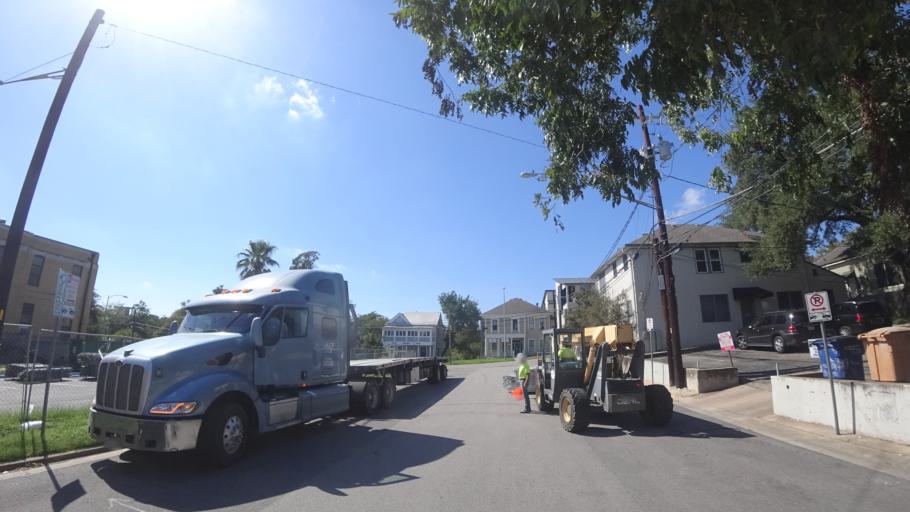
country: US
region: Texas
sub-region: Travis County
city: Austin
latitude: 30.2776
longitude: -97.7474
